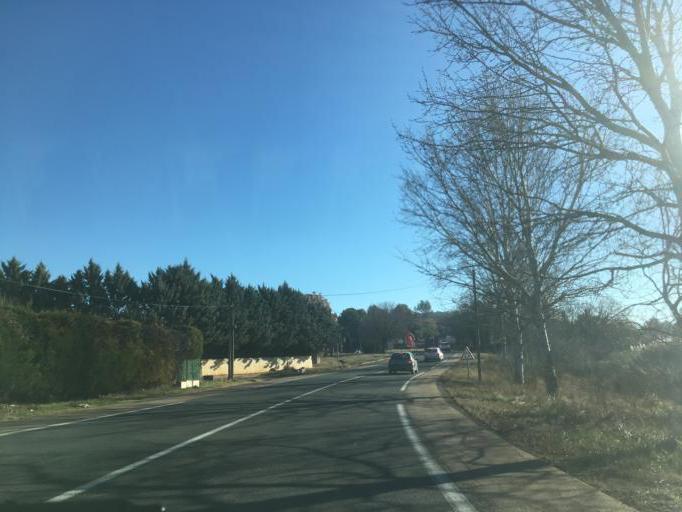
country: FR
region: Provence-Alpes-Cote d'Azur
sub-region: Departement du Var
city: Draguignan
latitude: 43.5275
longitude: 6.4352
